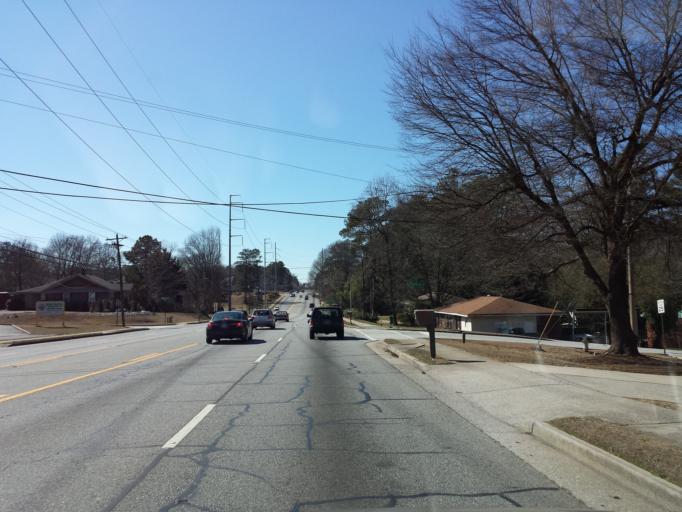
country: US
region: Georgia
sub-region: Cobb County
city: Fair Oaks
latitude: 33.8949
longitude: -84.5621
